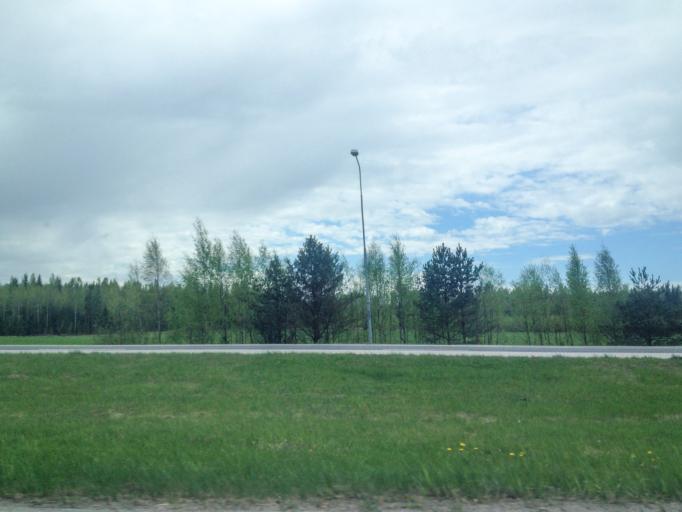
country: FI
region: Uusimaa
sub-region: Helsinki
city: Hyvinge
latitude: 60.5588
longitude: 24.8276
